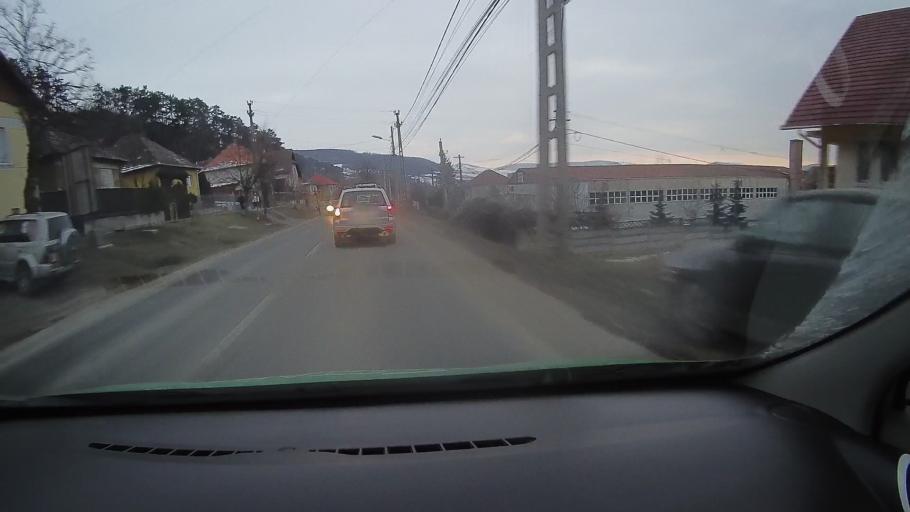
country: RO
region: Harghita
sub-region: Municipiul Odorheiu Secuiesc
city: Odorheiu Secuiesc
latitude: 46.2941
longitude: 25.2895
